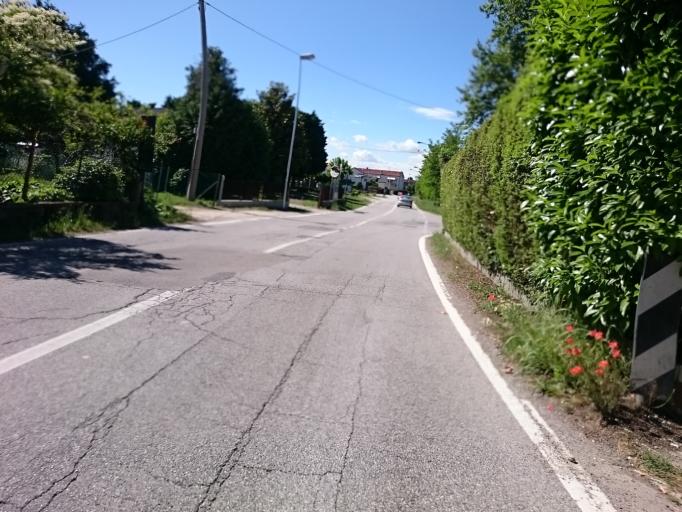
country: IT
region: Veneto
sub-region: Provincia di Padova
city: Piove di Sacco-Piovega
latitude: 45.2855
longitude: 12.0409
